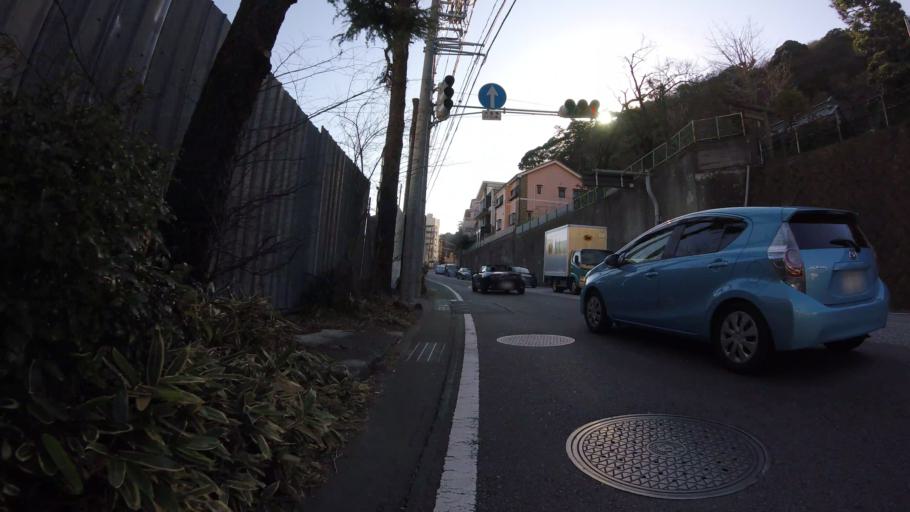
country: JP
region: Shizuoka
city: Atami
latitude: 35.0904
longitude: 139.0741
